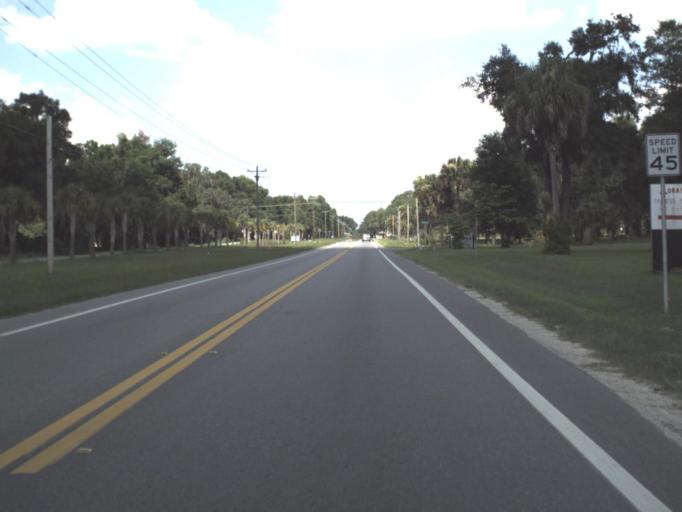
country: US
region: Florida
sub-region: Putnam County
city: Interlachen
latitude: 29.7325
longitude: -81.8876
